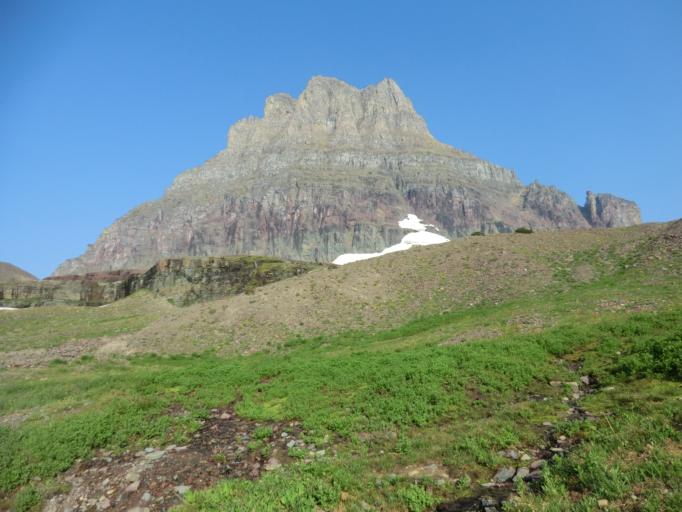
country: US
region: Montana
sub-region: Flathead County
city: Columbia Falls
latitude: 48.6909
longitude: -113.7312
